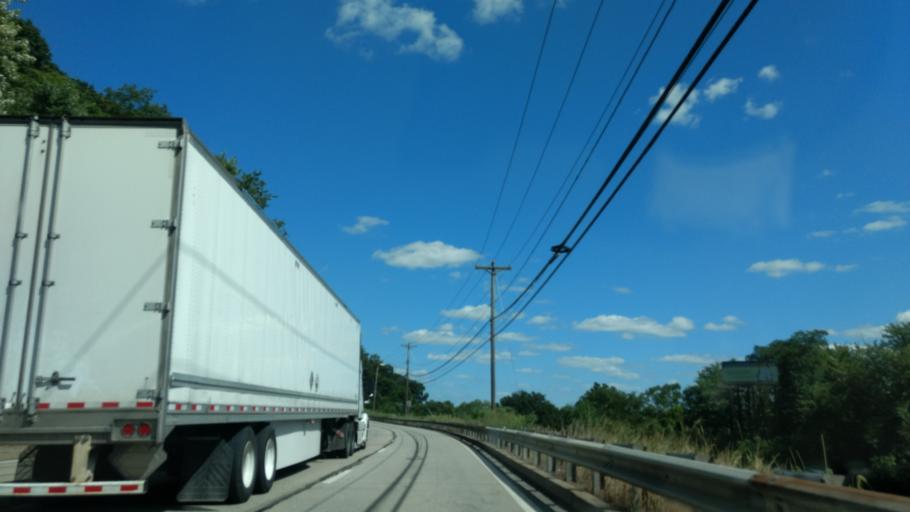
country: US
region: Pennsylvania
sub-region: Allegheny County
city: Coraopolis
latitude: 40.5234
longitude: -80.1508
